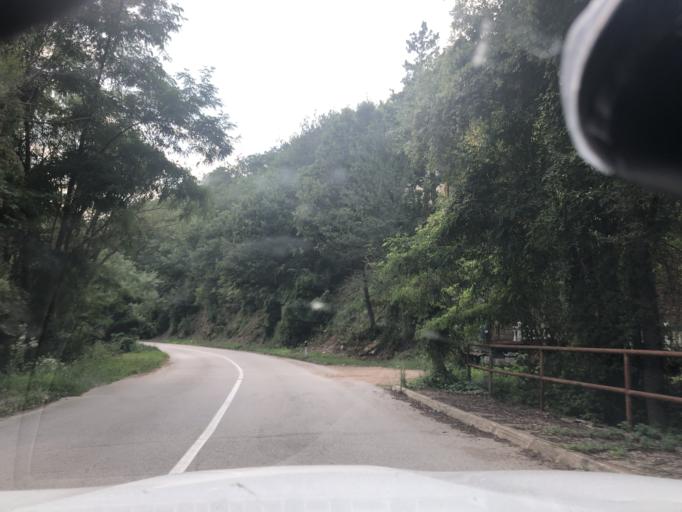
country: RS
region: Central Serbia
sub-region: Jablanicki Okrug
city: Medvega
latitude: 42.7816
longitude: 21.5964
